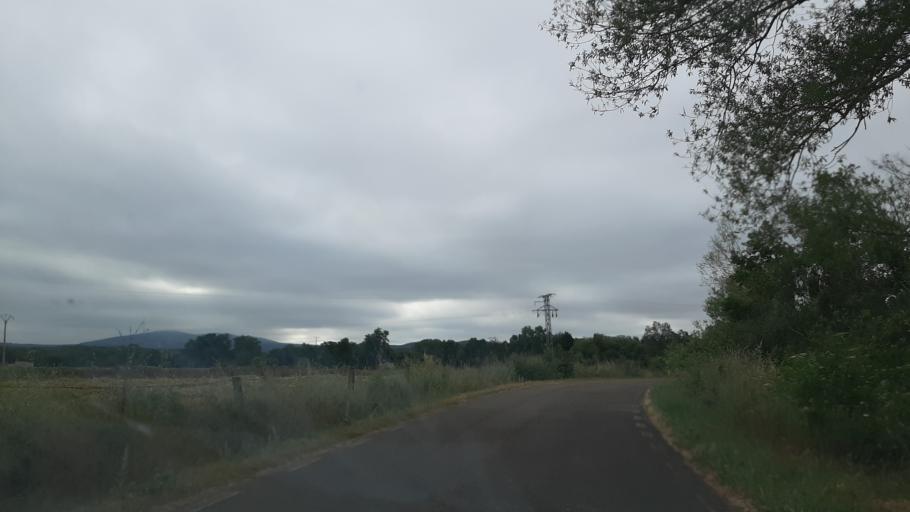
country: ES
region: Castille and Leon
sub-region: Provincia de Salamanca
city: Pastores
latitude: 40.5654
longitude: -6.4865
